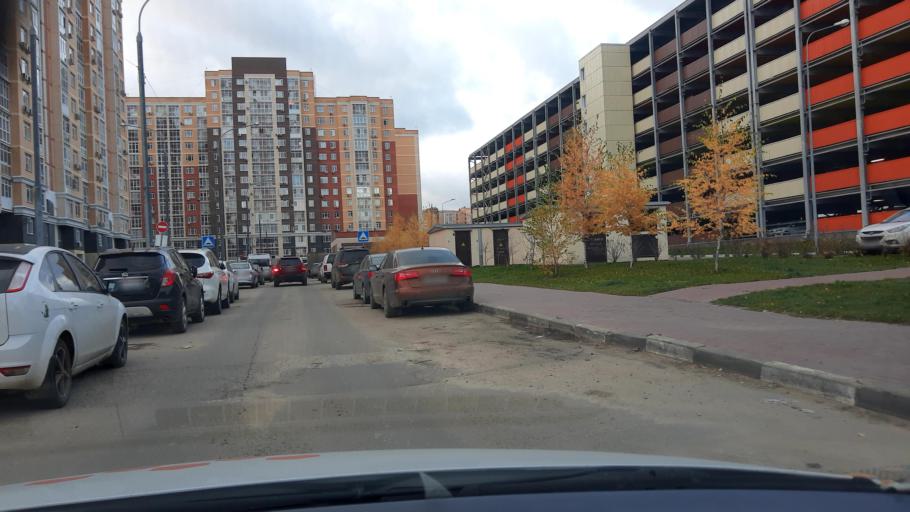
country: RU
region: Moskovskaya
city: Kommunarka
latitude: 55.5690
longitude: 37.4940
